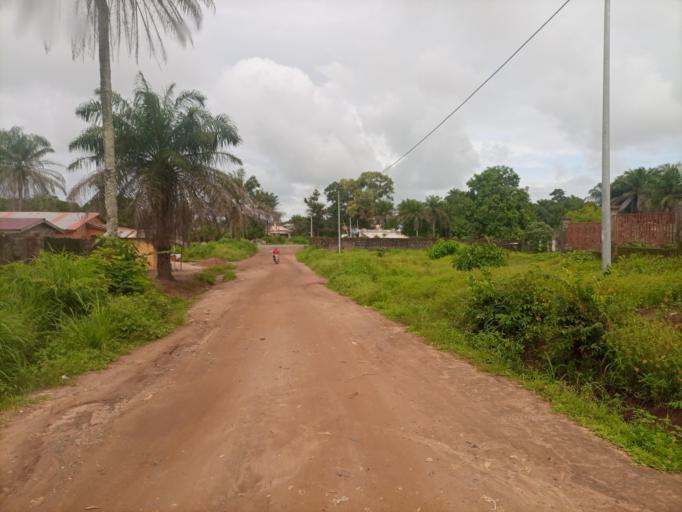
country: SL
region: Northern Province
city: Masoyila
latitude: 8.5958
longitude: -13.1688
